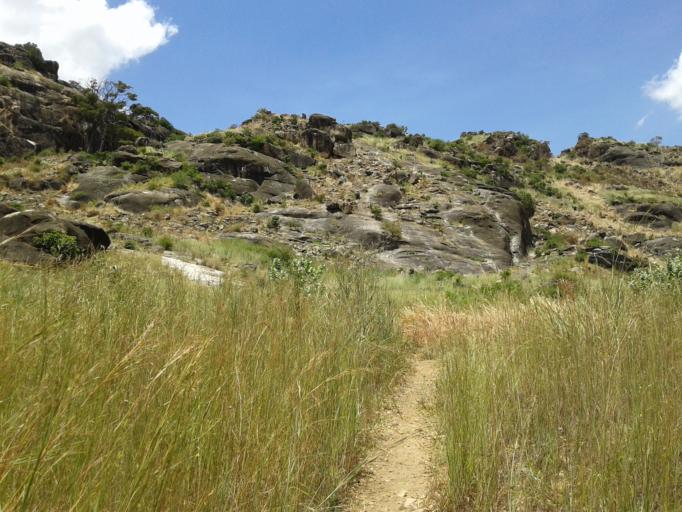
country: SS
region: Central Equatoria
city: Juba
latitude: 4.8456
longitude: 31.5506
